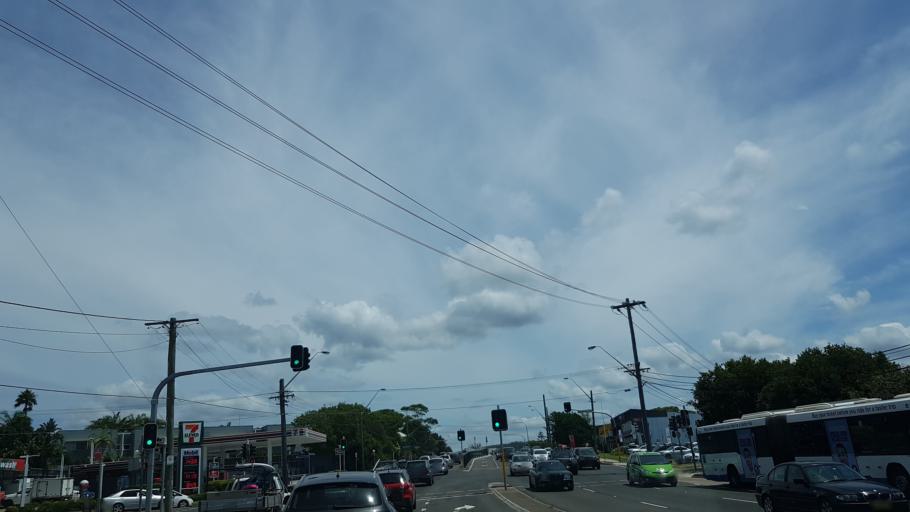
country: AU
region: New South Wales
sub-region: Pittwater
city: Warriewood
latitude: -33.6764
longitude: 151.3090
